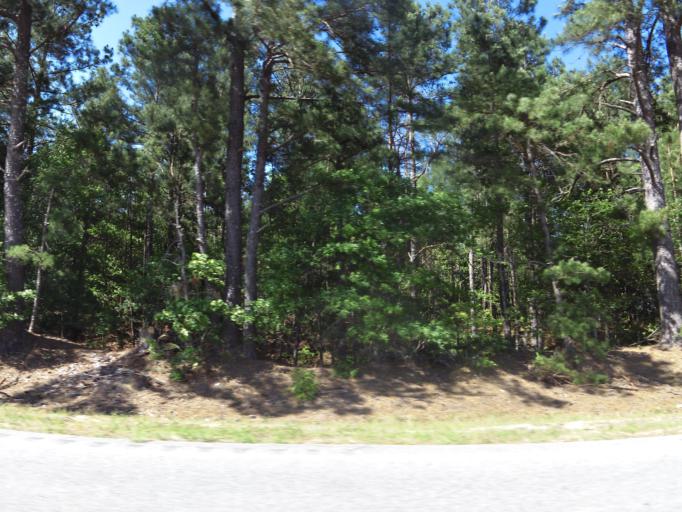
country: US
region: South Carolina
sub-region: Barnwell County
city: Blackville
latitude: 33.3611
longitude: -81.3043
